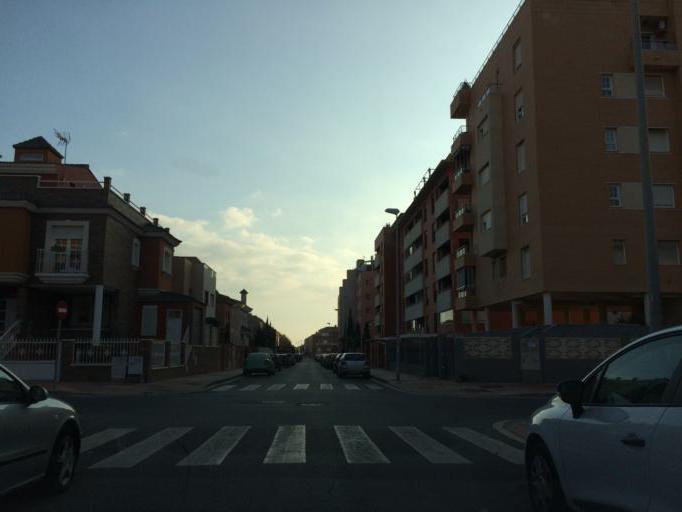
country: ES
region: Andalusia
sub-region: Provincia de Almeria
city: Almeria
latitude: 36.8239
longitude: -2.4386
